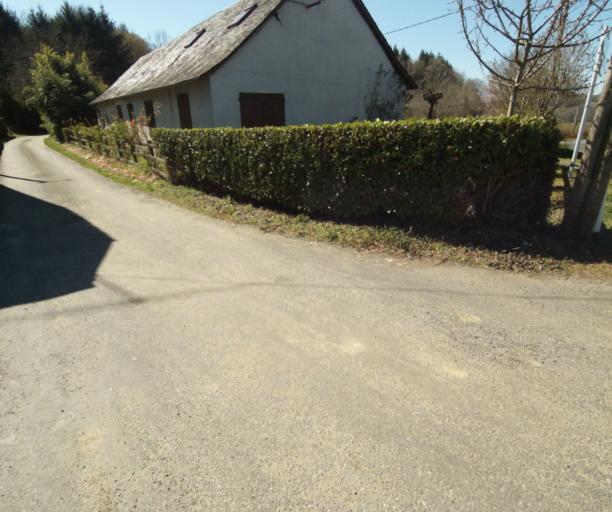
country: FR
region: Limousin
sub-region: Departement de la Correze
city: Chamboulive
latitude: 45.4607
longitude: 1.6690
